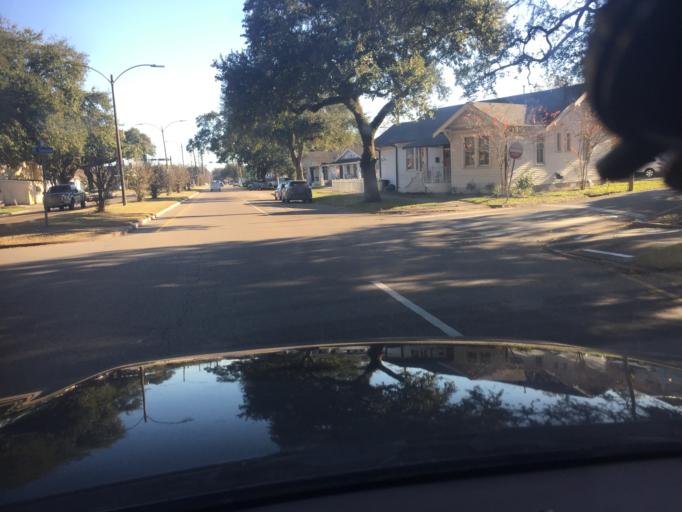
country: US
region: Louisiana
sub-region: Orleans Parish
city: New Orleans
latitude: 29.9864
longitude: -90.0736
